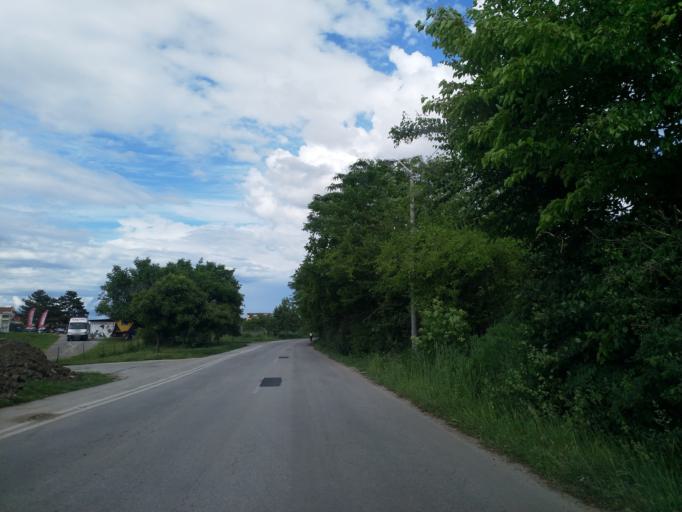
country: RS
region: Central Serbia
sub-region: Pomoravski Okrug
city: Jagodina
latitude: 43.9666
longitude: 21.2686
